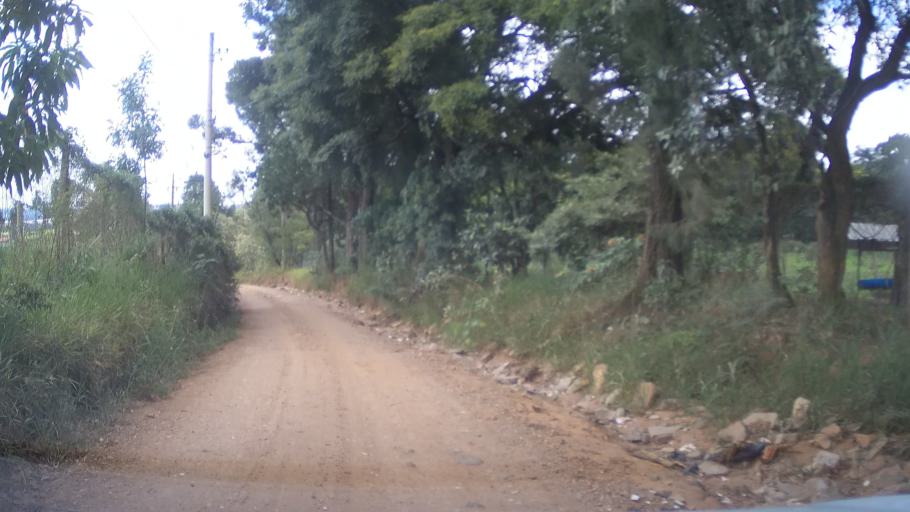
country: BR
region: Sao Paulo
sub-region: Itupeva
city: Itupeva
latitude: -23.1729
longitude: -47.0082
